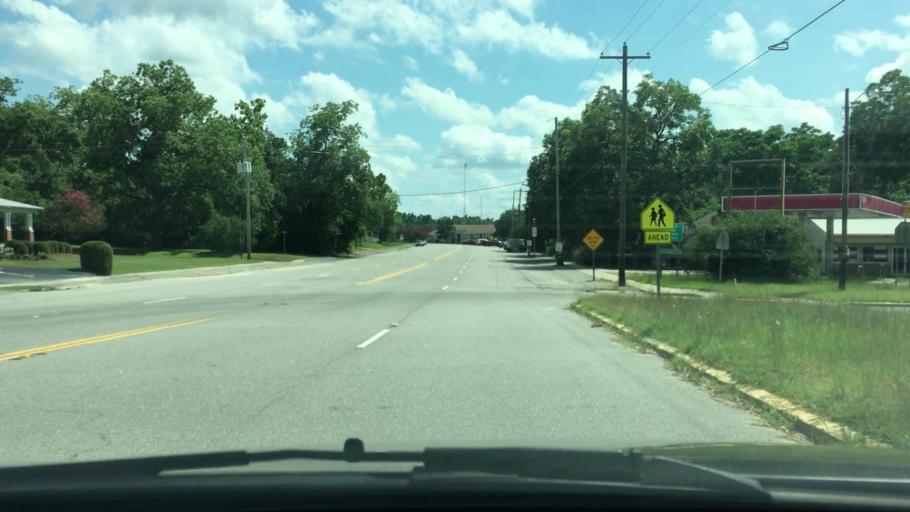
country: US
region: South Carolina
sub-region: Barnwell County
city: Williston
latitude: 33.6493
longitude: -81.3632
